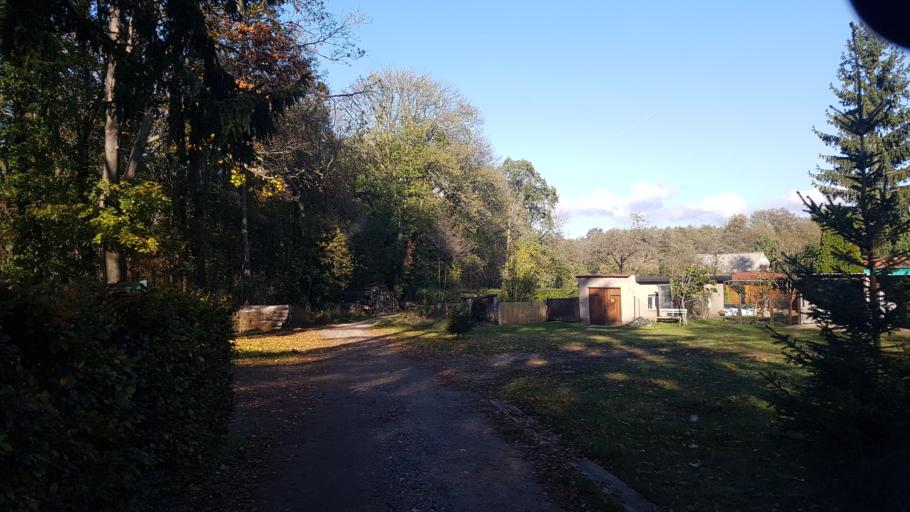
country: DE
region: Brandenburg
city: Doberlug-Kirchhain
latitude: 51.6365
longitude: 13.5329
